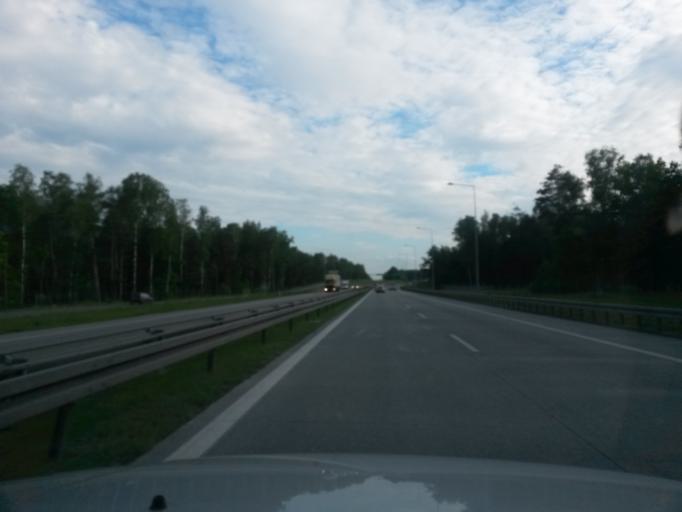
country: PL
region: Lodz Voivodeship
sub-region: Powiat tomaszowski
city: Tomaszow Mazowiecki
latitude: 51.5708
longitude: 20.0256
